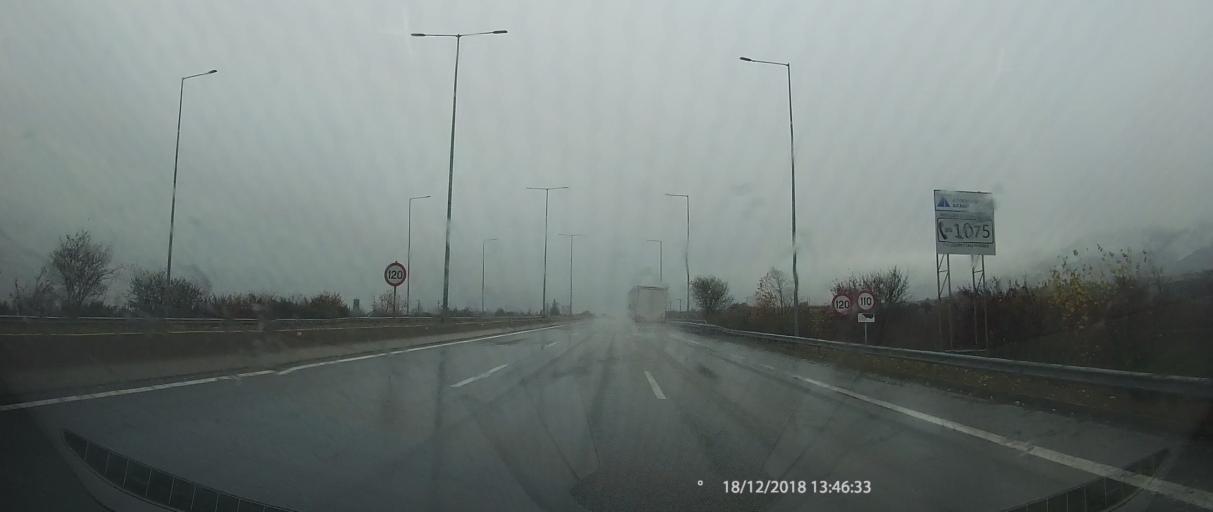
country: GR
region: Central Macedonia
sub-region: Nomos Pierias
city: Leptokarya
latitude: 40.0953
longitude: 22.5551
